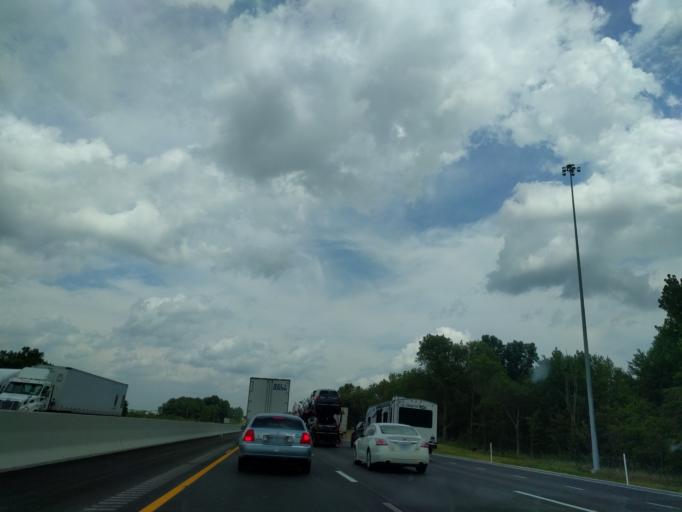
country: US
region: Kentucky
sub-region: Larue County
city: Hodgenville
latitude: 37.5267
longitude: -85.8837
